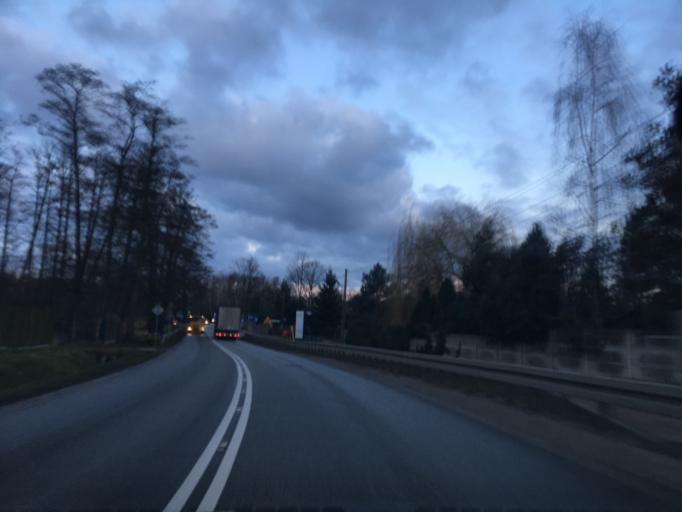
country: PL
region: Masovian Voivodeship
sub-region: Powiat grodziski
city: Milanowek
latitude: 52.0938
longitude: 20.6645
